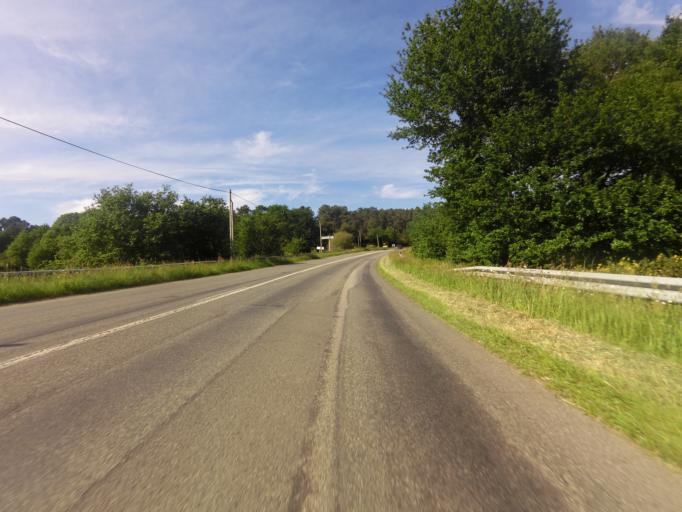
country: FR
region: Brittany
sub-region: Departement du Morbihan
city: Pluherlin
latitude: 47.7039
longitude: -2.3612
